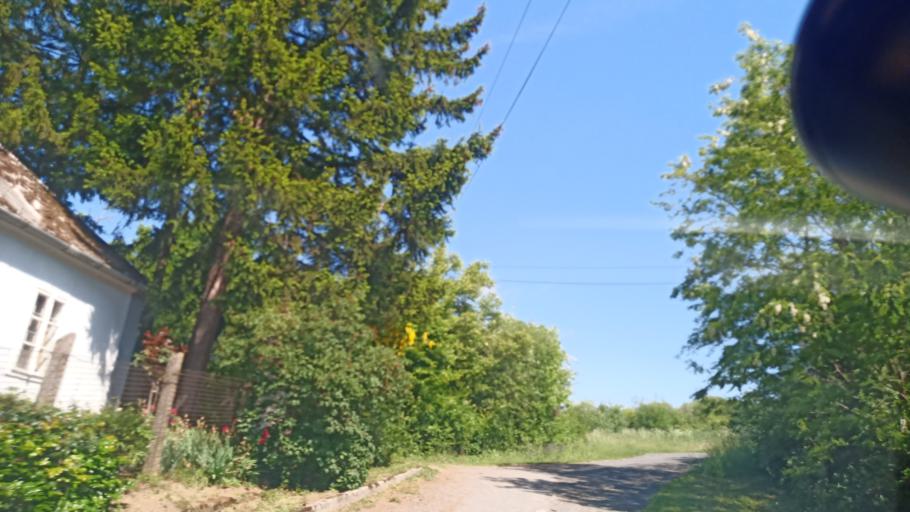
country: HU
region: Zala
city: Pacsa
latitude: 46.6553
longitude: 17.0611
